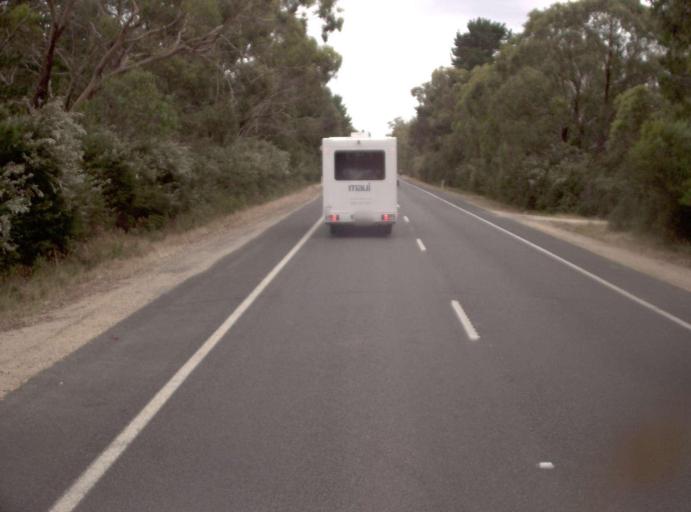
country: AU
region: Victoria
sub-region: Wellington
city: Sale
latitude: -38.1936
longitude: 147.0788
